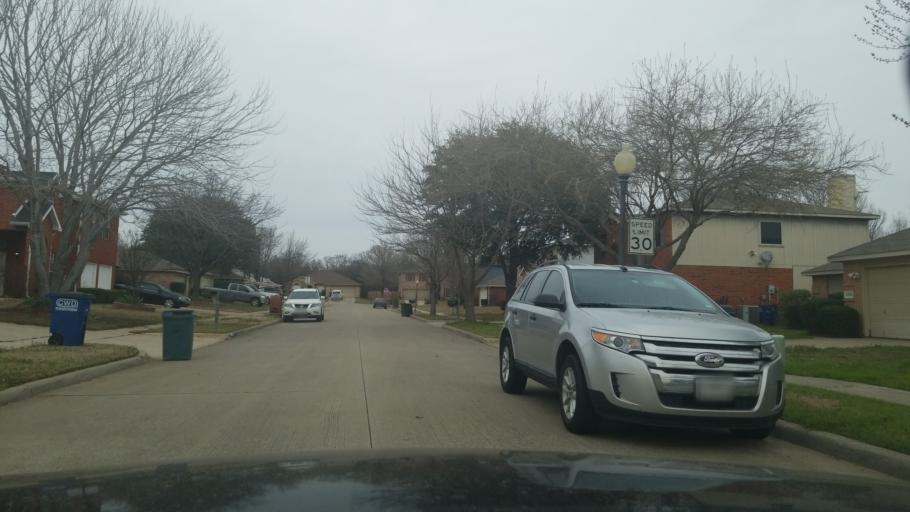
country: US
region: Texas
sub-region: Denton County
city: Hickory Creek
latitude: 33.1313
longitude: -97.0565
